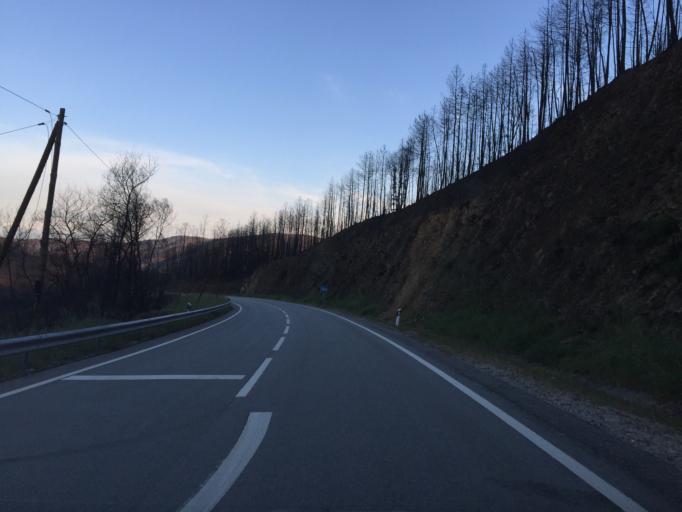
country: PT
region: Coimbra
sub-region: Pampilhosa da Serra
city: Pampilhosa da Serra
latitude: 40.0688
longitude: -7.9717
